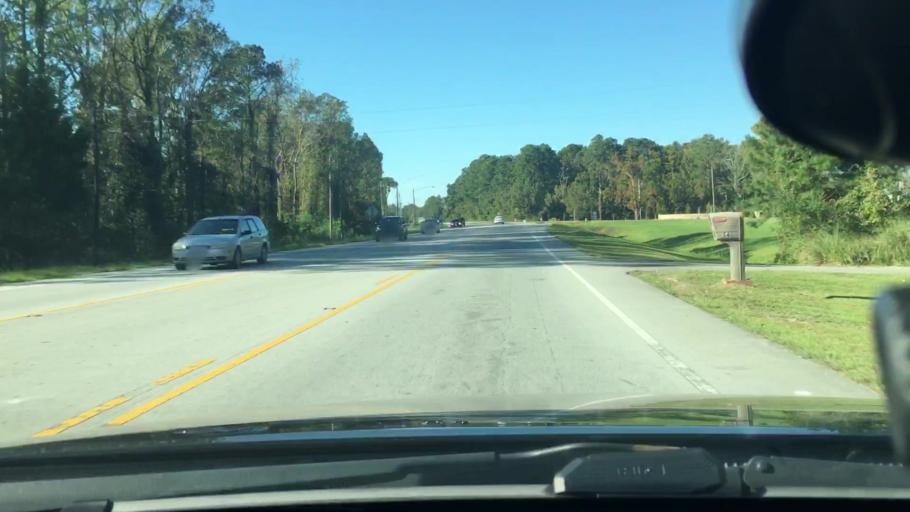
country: US
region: North Carolina
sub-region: Craven County
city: Trent Woods
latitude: 35.1502
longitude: -77.1090
